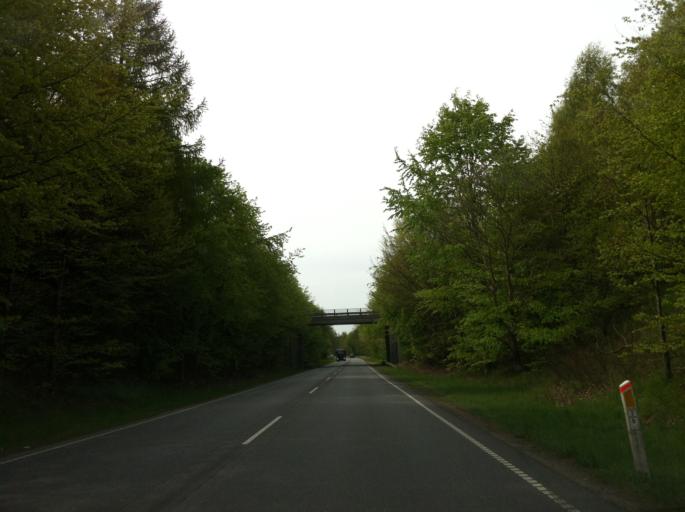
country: DK
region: Capital Region
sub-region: Hillerod Kommune
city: Hillerod
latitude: 55.9185
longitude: 12.3236
